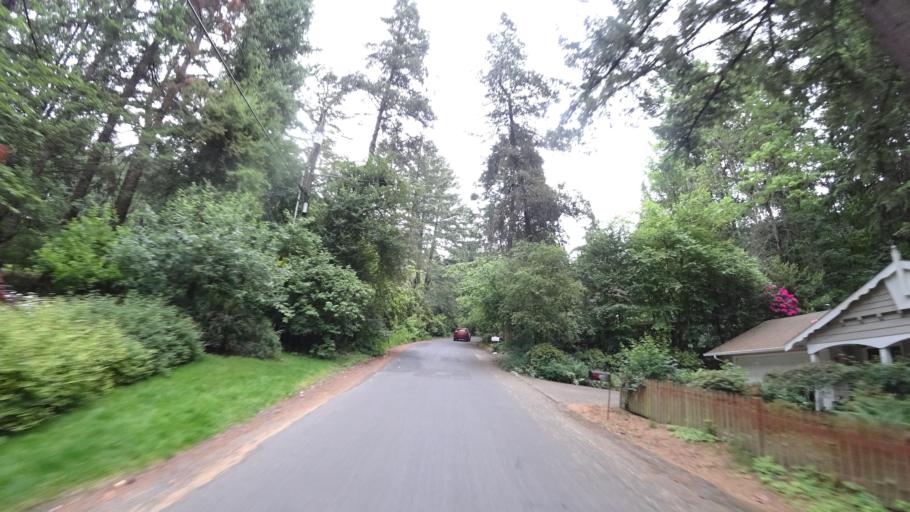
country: US
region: Oregon
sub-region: Multnomah County
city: Portland
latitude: 45.4848
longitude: -122.6994
